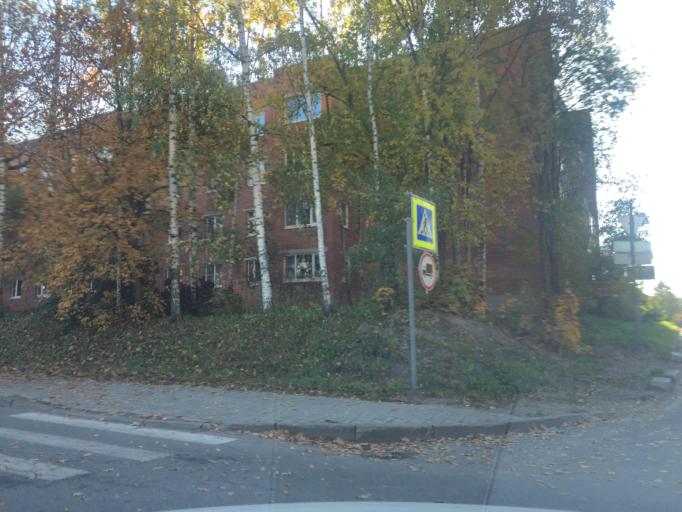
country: RU
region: Leningrad
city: Priozersk
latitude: 61.0352
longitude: 30.1123
